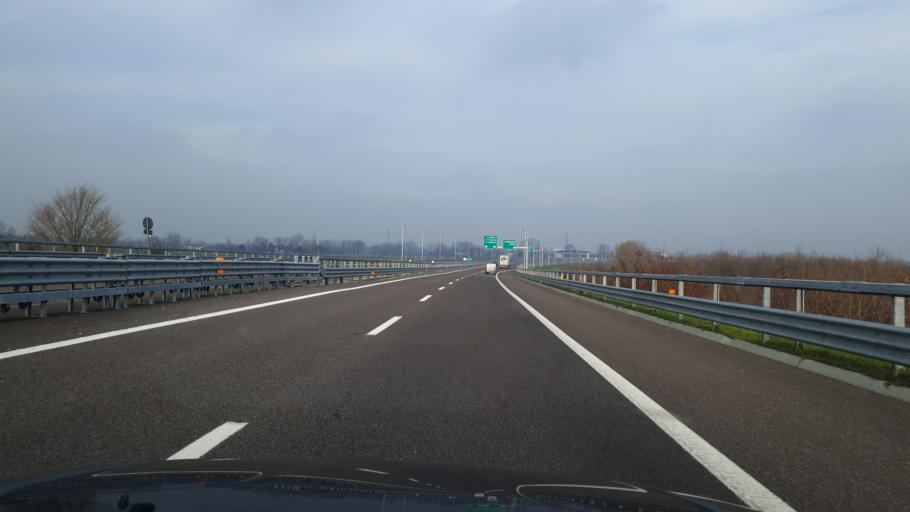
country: IT
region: Veneto
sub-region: Provincia di Padova
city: Santa Margherita d'Adige
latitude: 45.2058
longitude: 11.5427
